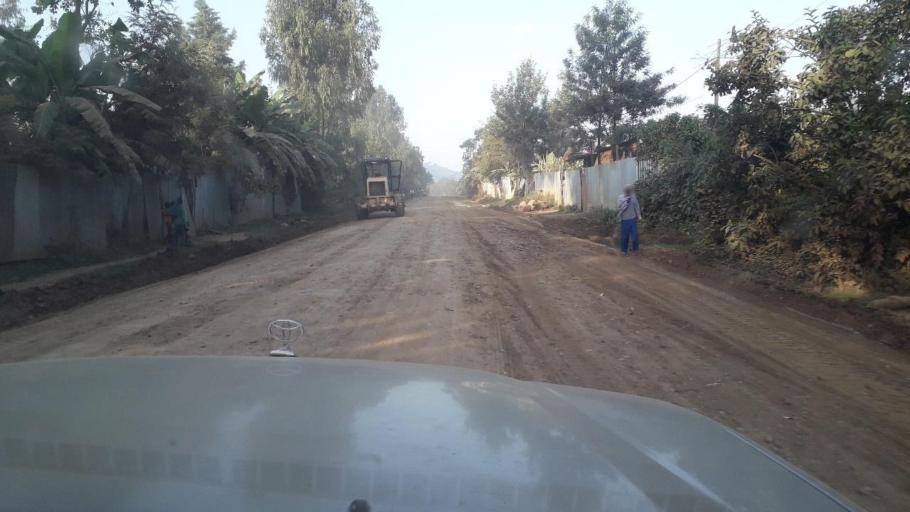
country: ET
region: Oromiya
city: Jima
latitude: 7.6302
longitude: 36.8298
